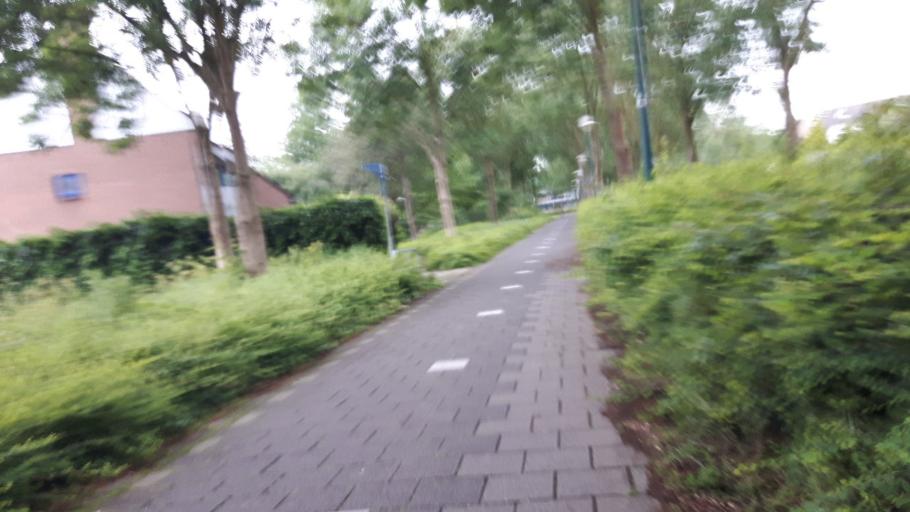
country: NL
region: Utrecht
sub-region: Gemeente Woerden
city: Woerden
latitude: 52.0785
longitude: 4.8701
